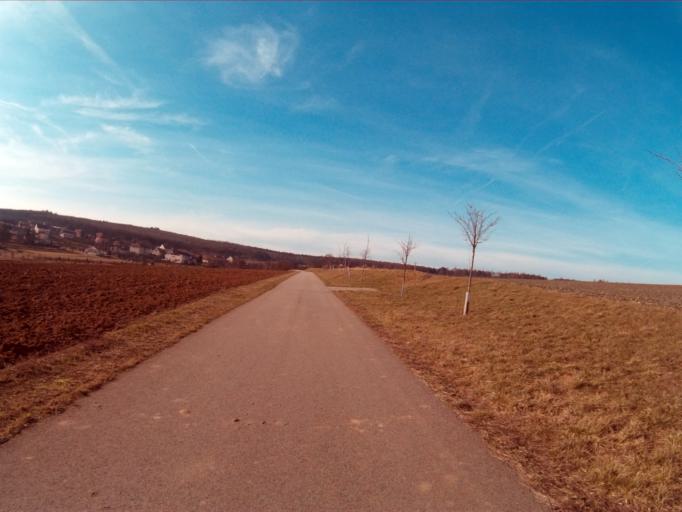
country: CZ
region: Vysocina
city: Mohelno
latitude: 49.1448
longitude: 16.1789
